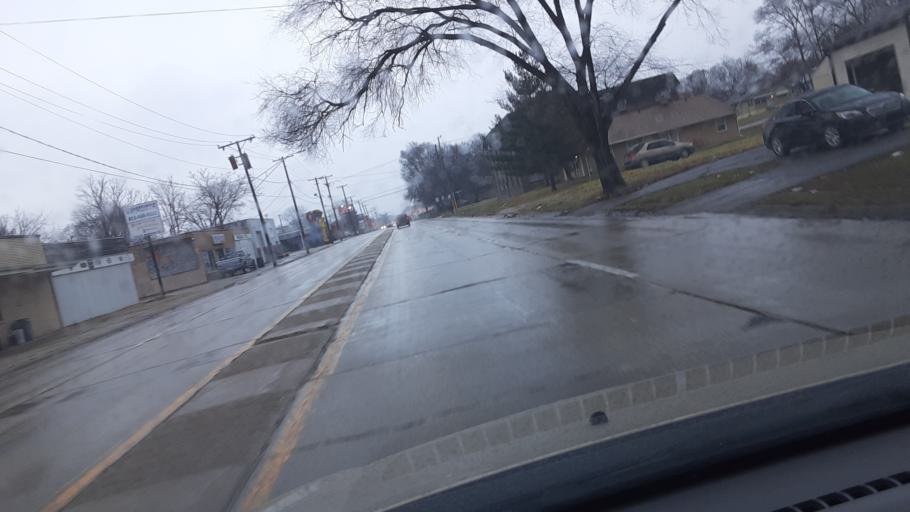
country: US
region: Illinois
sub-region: Winnebago County
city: Rockford
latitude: 42.2883
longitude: -89.1133
